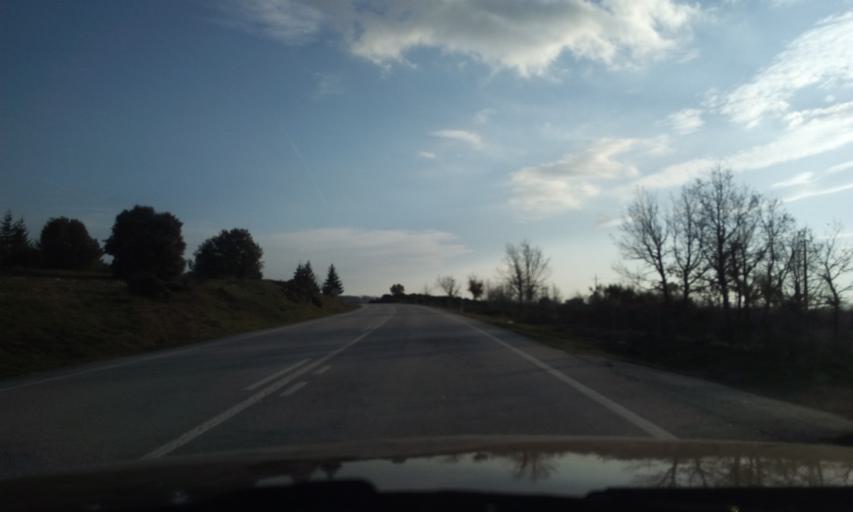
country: ES
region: Castille and Leon
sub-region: Provincia de Salamanca
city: Fuentes de Onoro
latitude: 40.6166
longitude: -6.9810
